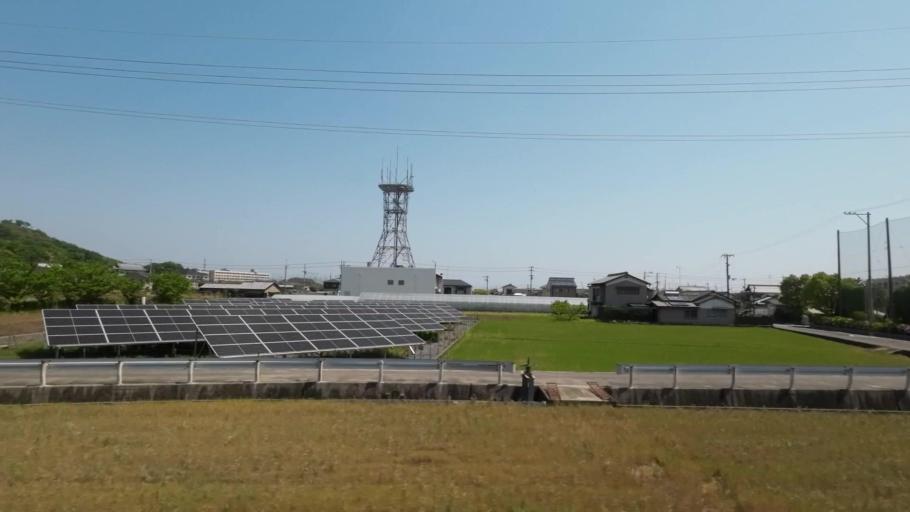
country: JP
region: Ehime
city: Saijo
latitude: 34.0174
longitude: 133.0318
